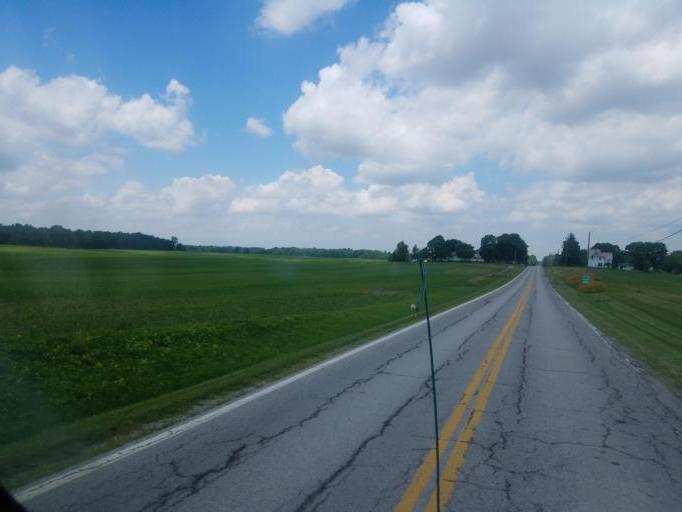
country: US
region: Ohio
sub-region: Huron County
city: Willard
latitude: 41.0695
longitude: -82.6836
